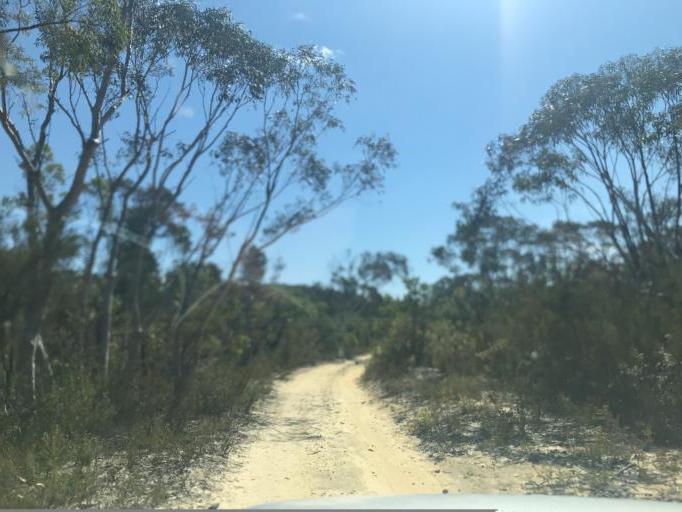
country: AU
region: New South Wales
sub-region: Wyong Shire
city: Little Jilliby
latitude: -33.1592
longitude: 151.0989
